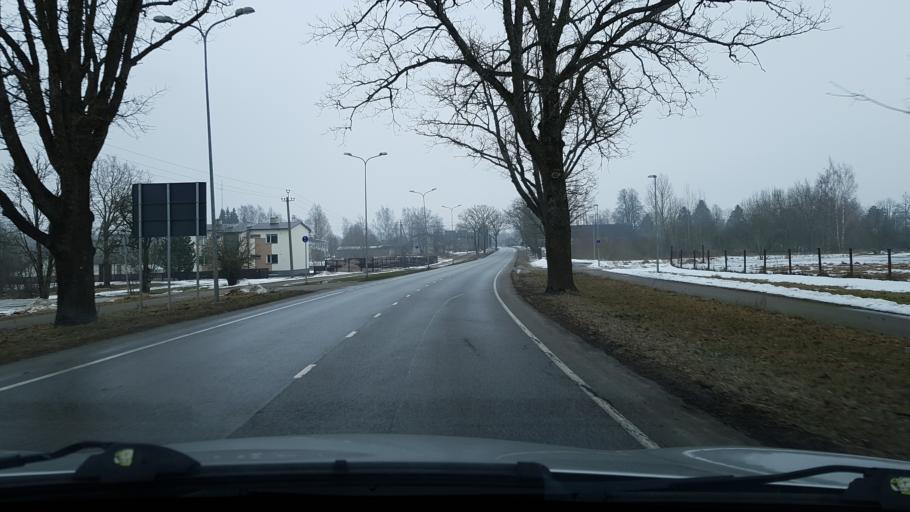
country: EE
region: Viljandimaa
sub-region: Viiratsi vald
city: Viiratsi
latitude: 58.2428
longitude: 25.8562
